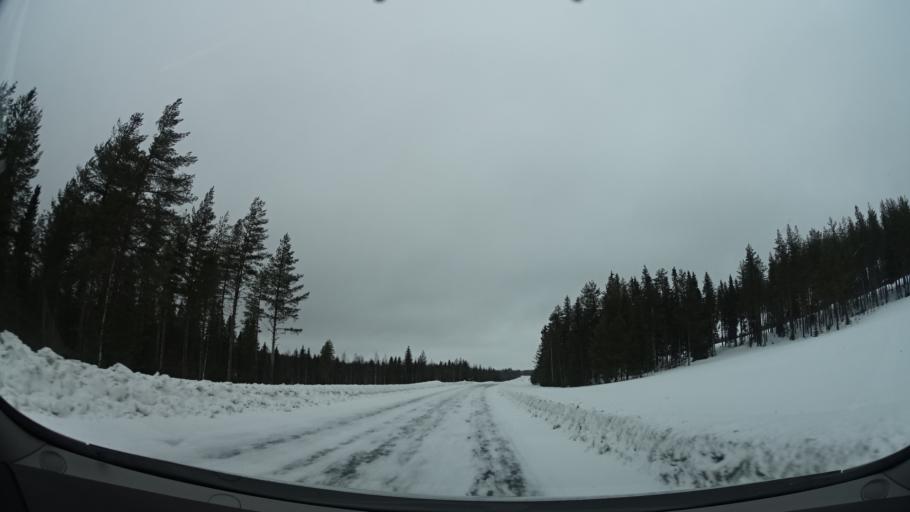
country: SE
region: Vaesterbotten
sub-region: Mala Kommun
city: Mala
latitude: 65.1070
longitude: 18.8913
